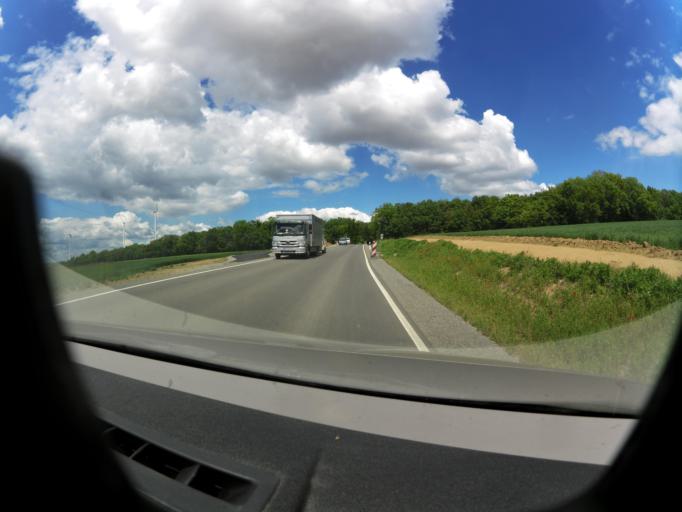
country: DE
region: Bavaria
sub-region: Regierungsbezirk Unterfranken
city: Schwanfeld
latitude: 49.9322
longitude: 10.1374
